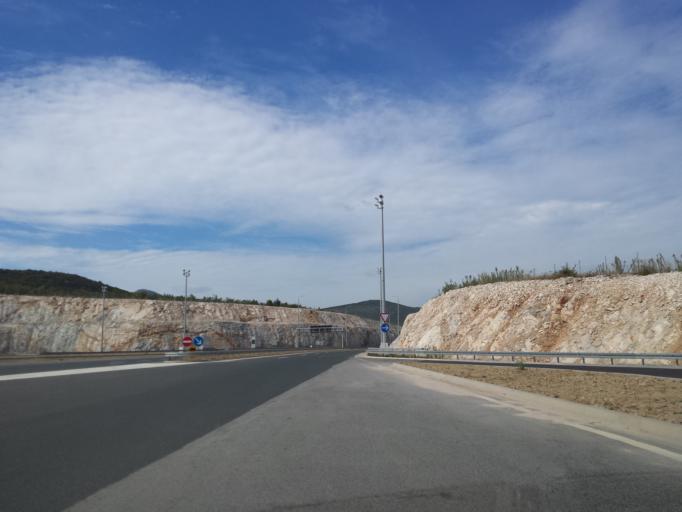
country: BA
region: Federation of Bosnia and Herzegovina
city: Ljubuski
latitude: 43.1232
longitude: 17.5737
